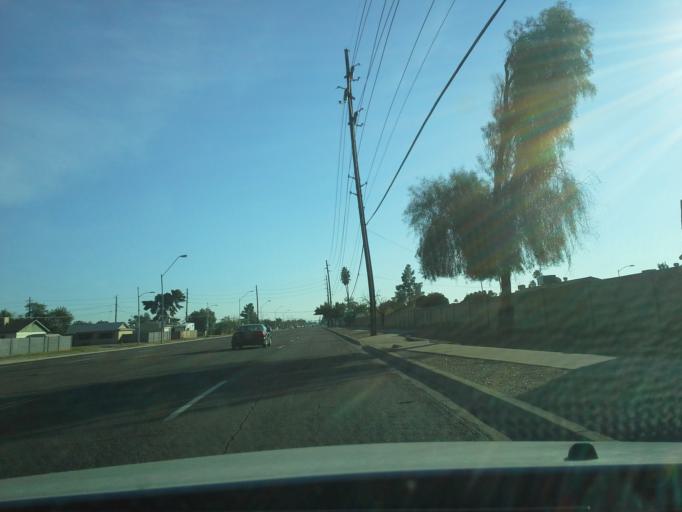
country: US
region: Arizona
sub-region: Maricopa County
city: Glendale
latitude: 33.6024
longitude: -112.1340
